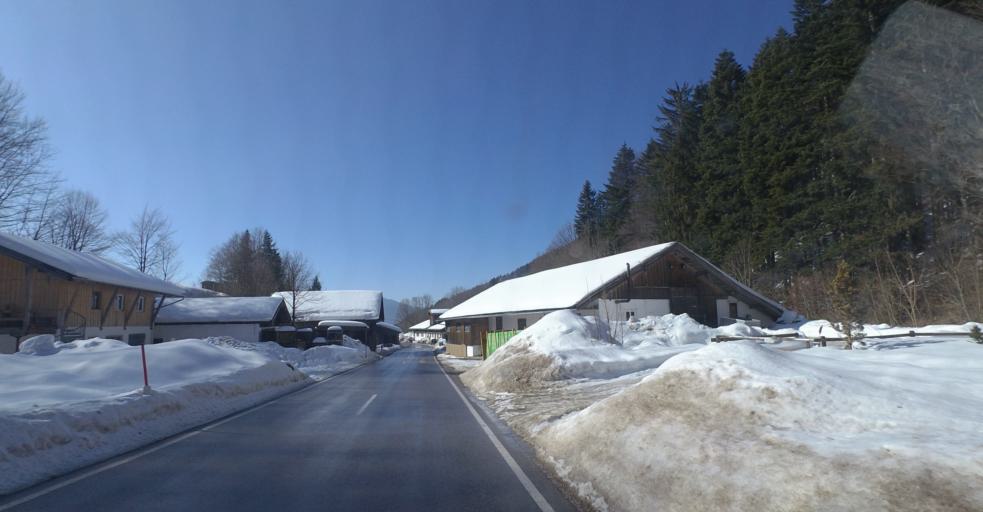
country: DE
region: Bavaria
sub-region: Upper Bavaria
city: Inzell
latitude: 47.7720
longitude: 12.7829
